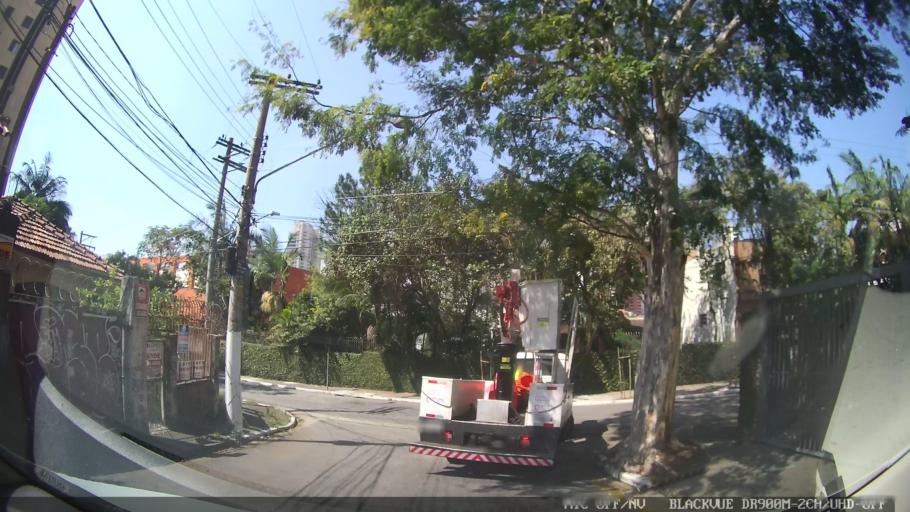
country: BR
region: Sao Paulo
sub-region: Sao Paulo
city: Sao Paulo
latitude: -23.4900
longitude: -46.6343
